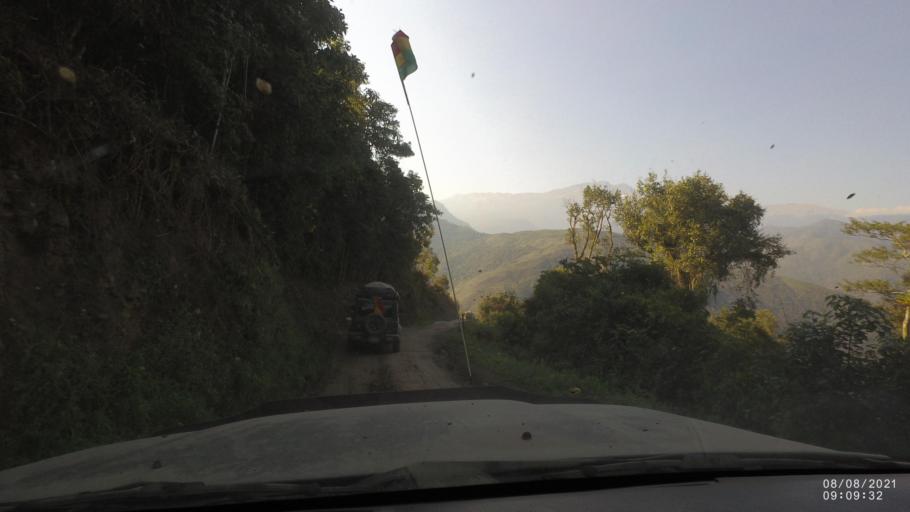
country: BO
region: La Paz
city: Quime
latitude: -16.5690
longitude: -66.7316
